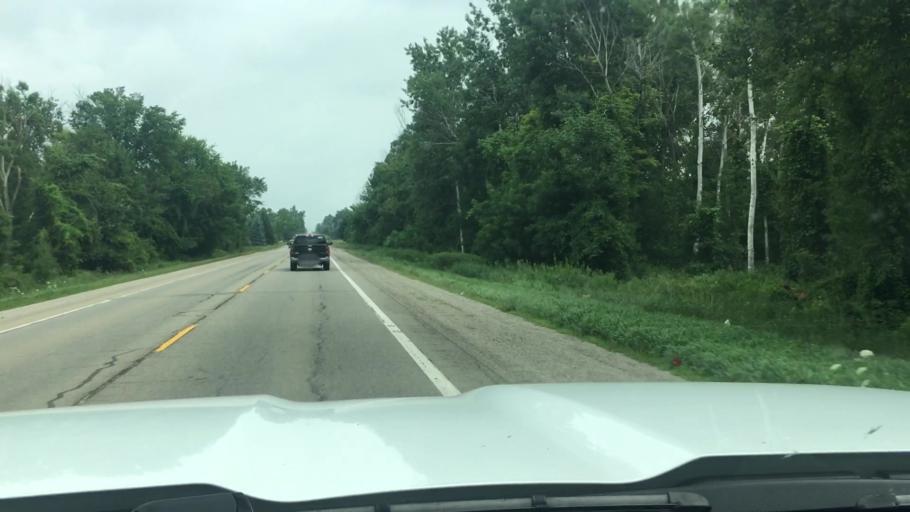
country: US
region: Michigan
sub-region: Sanilac County
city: Brown City
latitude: 43.1550
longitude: -83.0753
